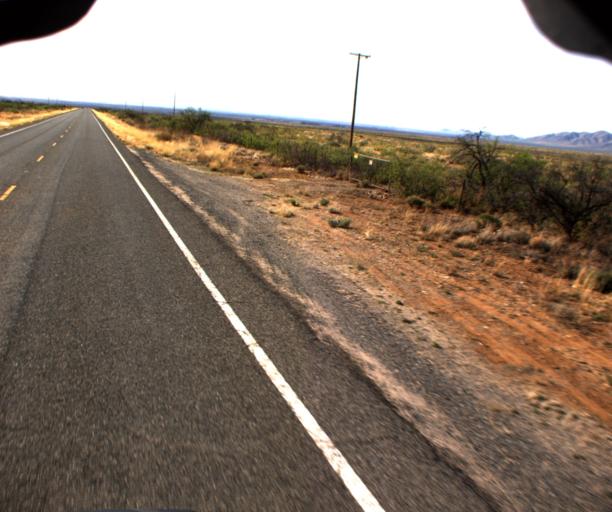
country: US
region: Arizona
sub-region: Cochise County
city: Willcox
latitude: 32.1875
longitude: -109.6813
